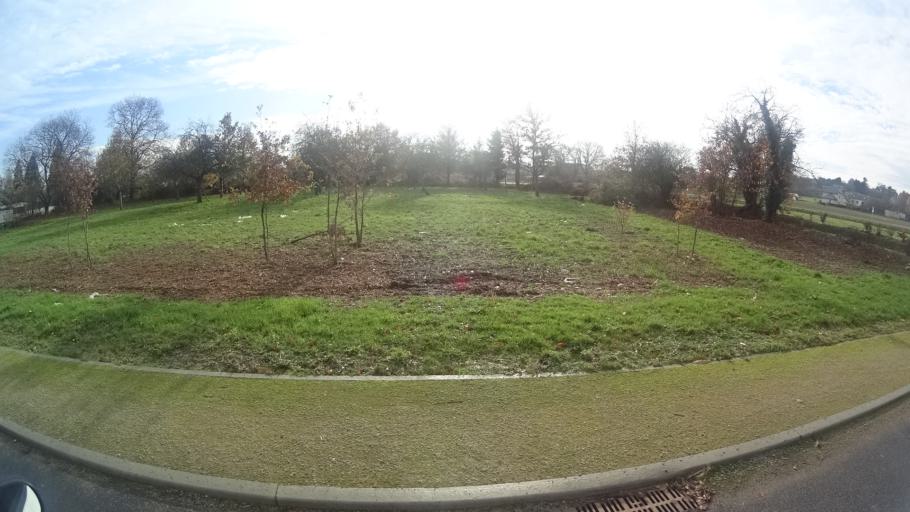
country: FR
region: Brittany
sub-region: Departement du Morbihan
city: Rieux
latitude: 47.6164
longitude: -2.1120
